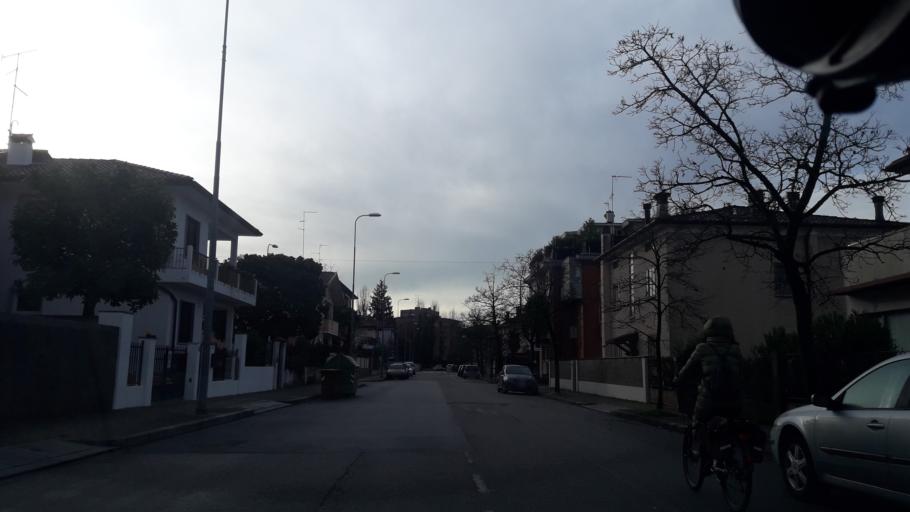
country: IT
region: Friuli Venezia Giulia
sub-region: Provincia di Udine
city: Udine
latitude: 46.0740
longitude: 13.2433
